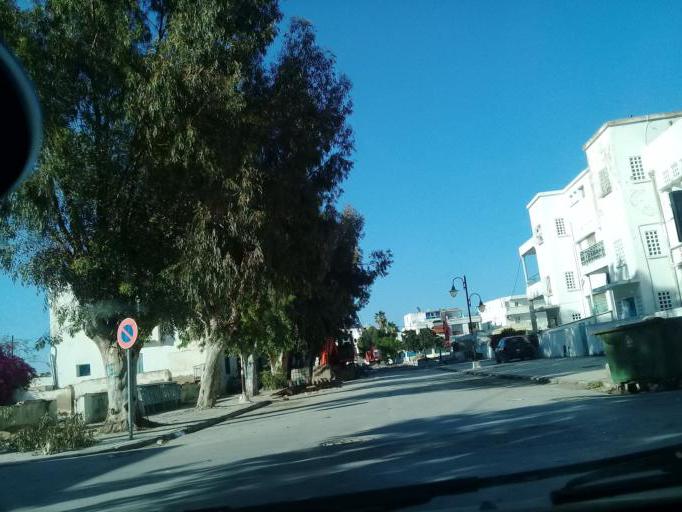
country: TN
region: Tunis
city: La Goulette
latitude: 36.8229
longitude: 10.3115
